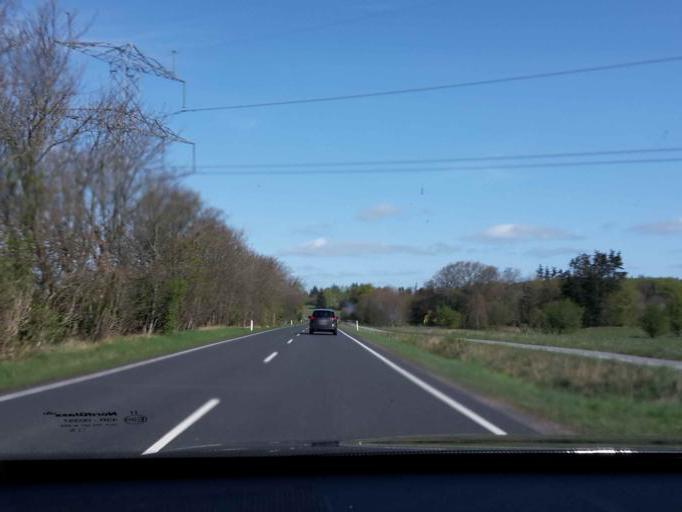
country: DK
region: South Denmark
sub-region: Vejen Kommune
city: Vejen
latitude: 55.5112
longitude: 9.1288
